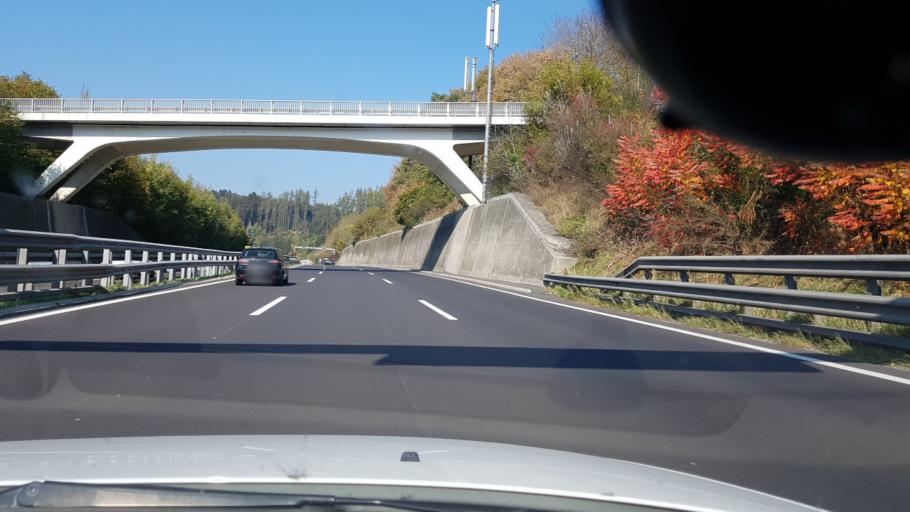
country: AT
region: Styria
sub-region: Politischer Bezirk Leoben
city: Leoben
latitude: 47.3658
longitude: 15.1076
